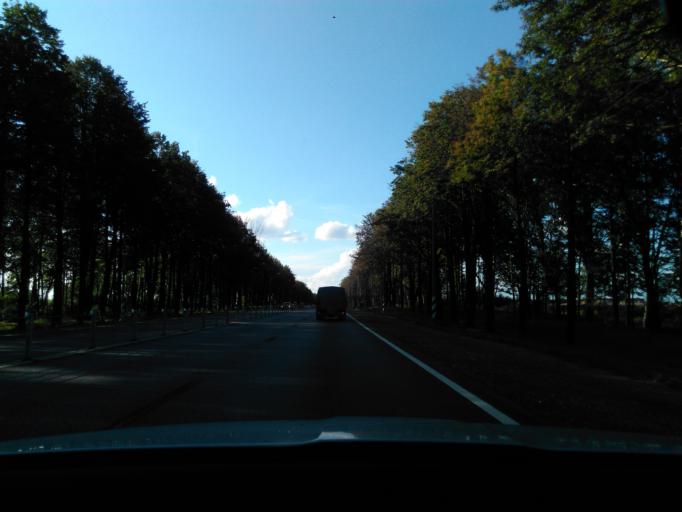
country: RU
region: Tverskaya
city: Zavidovo
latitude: 56.5667
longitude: 36.5040
